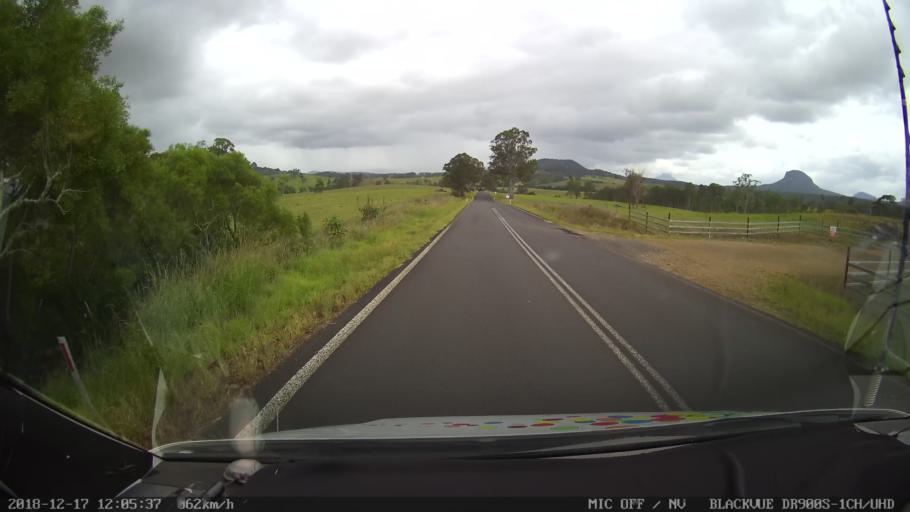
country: AU
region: New South Wales
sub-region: Kyogle
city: Kyogle
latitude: -28.4909
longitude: 152.5665
